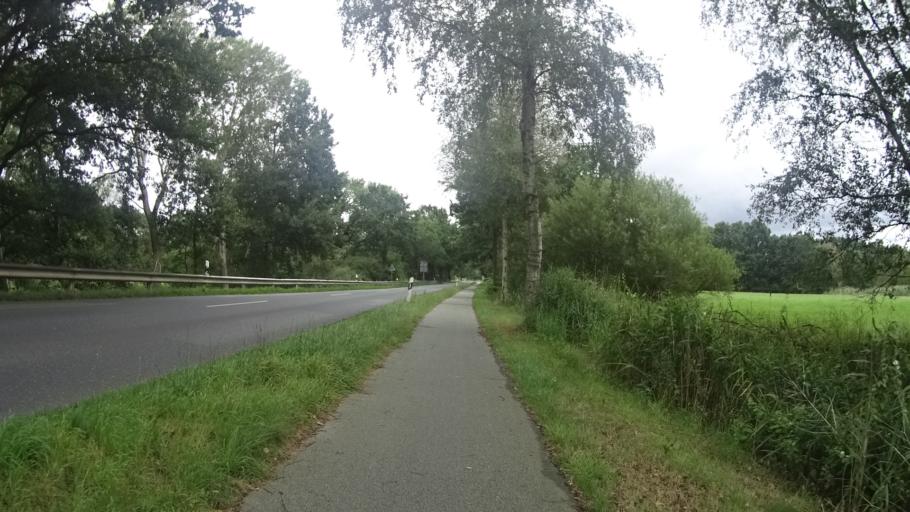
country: DE
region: Lower Saxony
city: Schiffdorf
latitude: 53.5357
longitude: 8.6694
